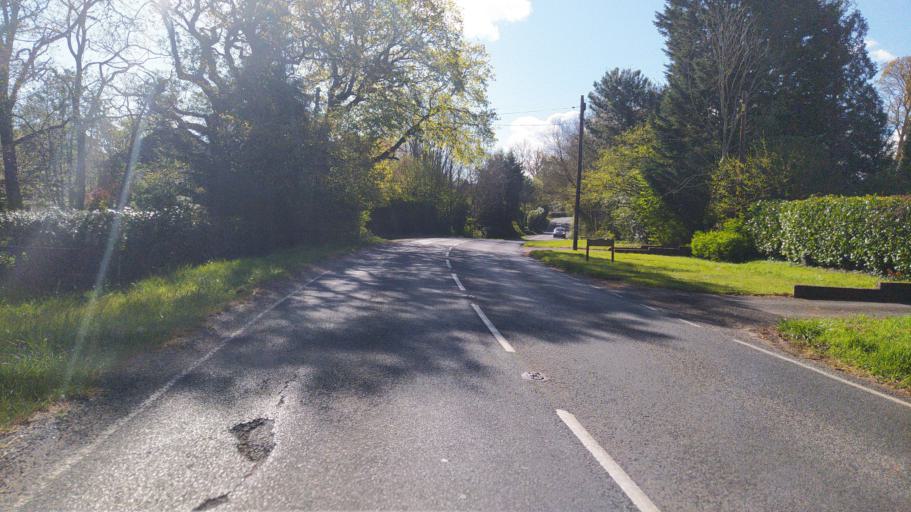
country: GB
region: England
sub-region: Hampshire
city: Hythe
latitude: 50.8726
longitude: -1.4232
